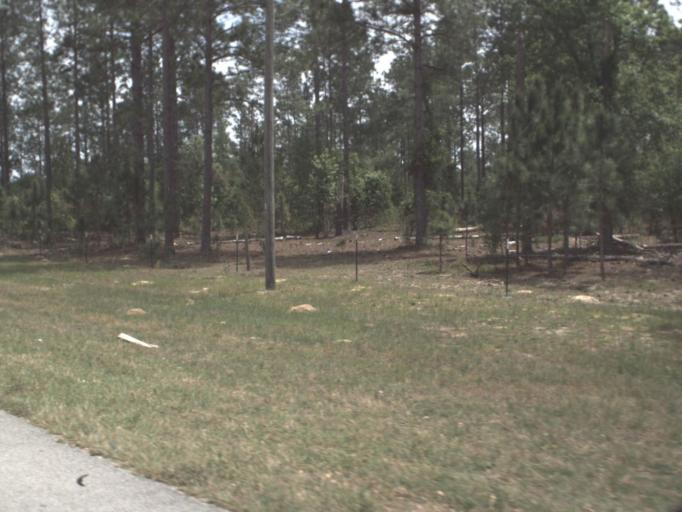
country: US
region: Florida
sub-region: Lake County
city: Mount Plymouth
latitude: 28.8516
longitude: -81.5458
